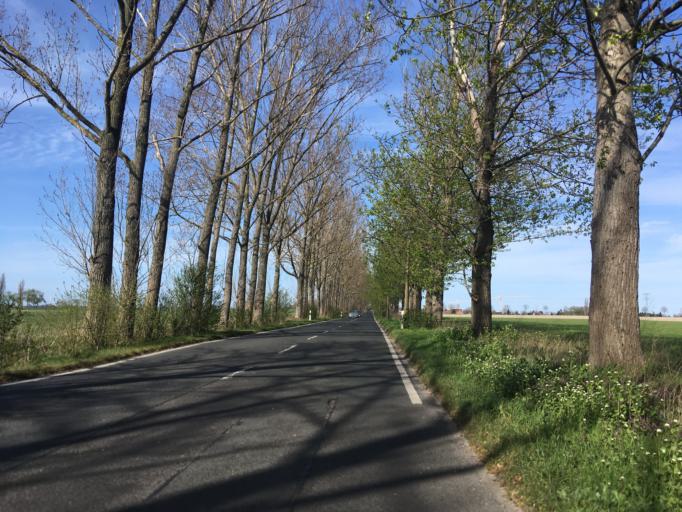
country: DE
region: Berlin
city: Wartenberg
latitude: 52.5853
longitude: 13.5235
